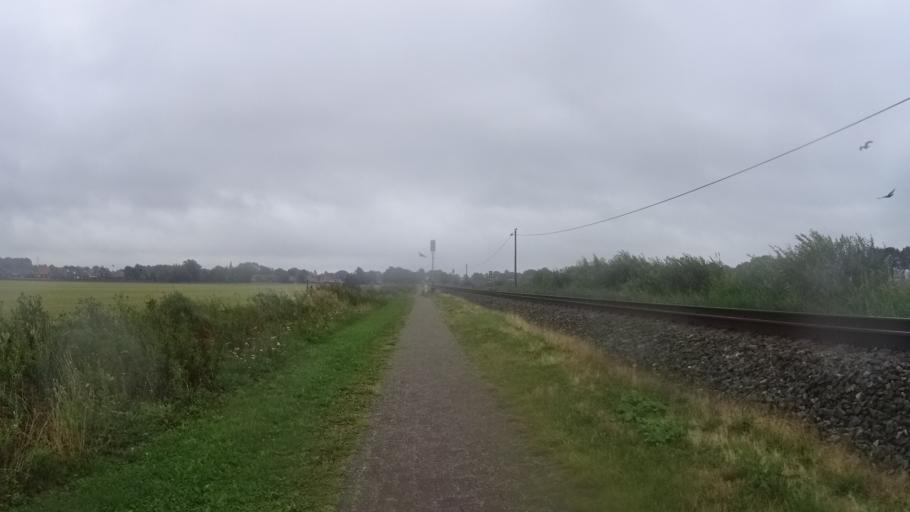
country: DE
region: Lower Saxony
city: Bunde
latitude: 53.1872
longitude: 7.2532
